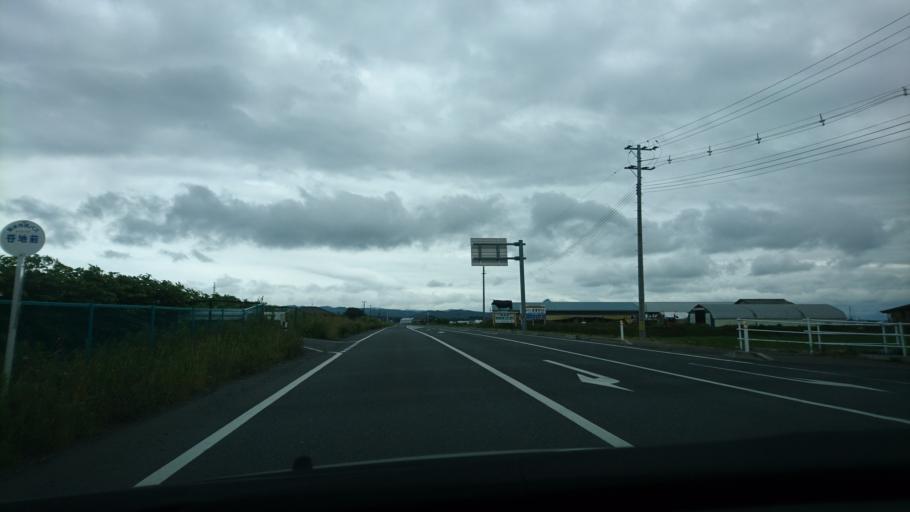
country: JP
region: Miyagi
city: Wakuya
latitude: 38.7200
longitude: 141.2552
